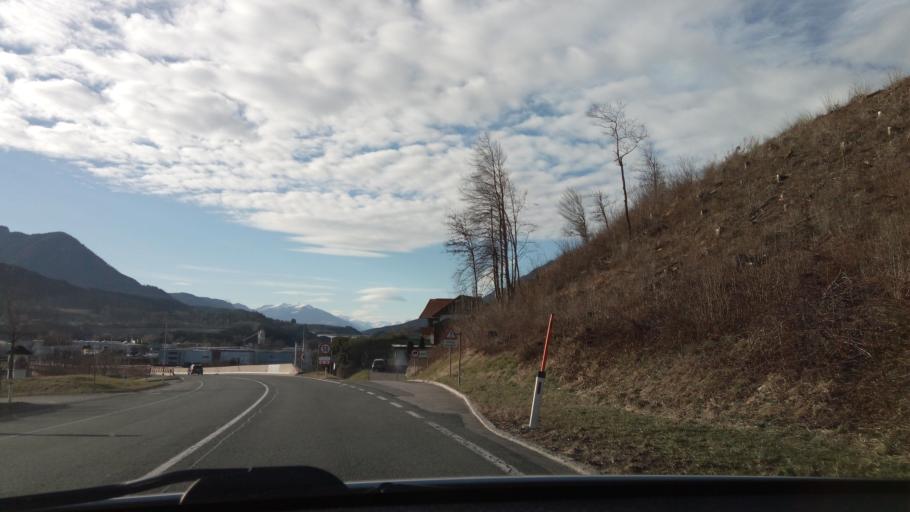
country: AT
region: Carinthia
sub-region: Villach Stadt
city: Villach
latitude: 46.6291
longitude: 13.8362
